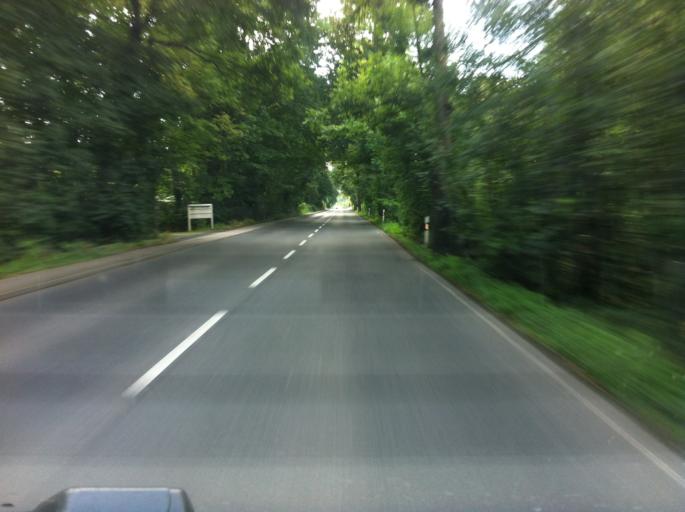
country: DE
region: North Rhine-Westphalia
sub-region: Regierungsbezirk Koln
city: Mengenich
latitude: 50.9736
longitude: 6.8624
